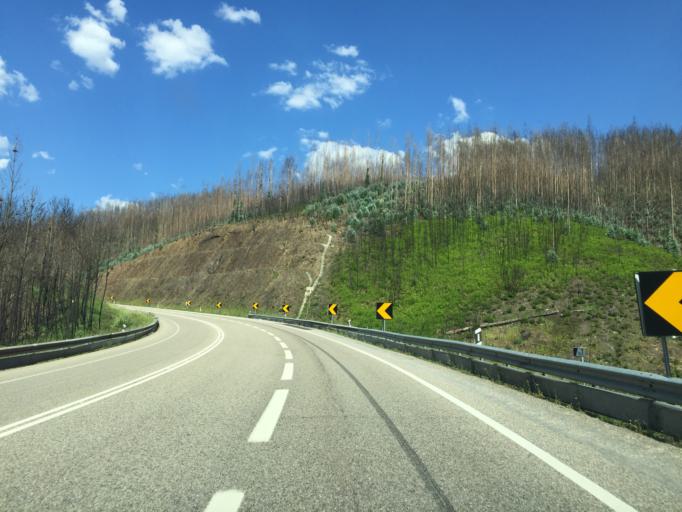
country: PT
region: Leiria
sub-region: Figueiro Dos Vinhos
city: Figueiro dos Vinhos
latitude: 39.9267
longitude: -8.3030
